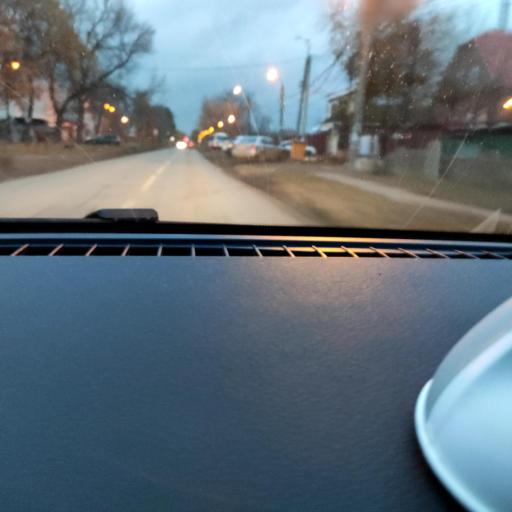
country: RU
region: Samara
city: Smyshlyayevka
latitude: 53.2451
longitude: 50.3374
